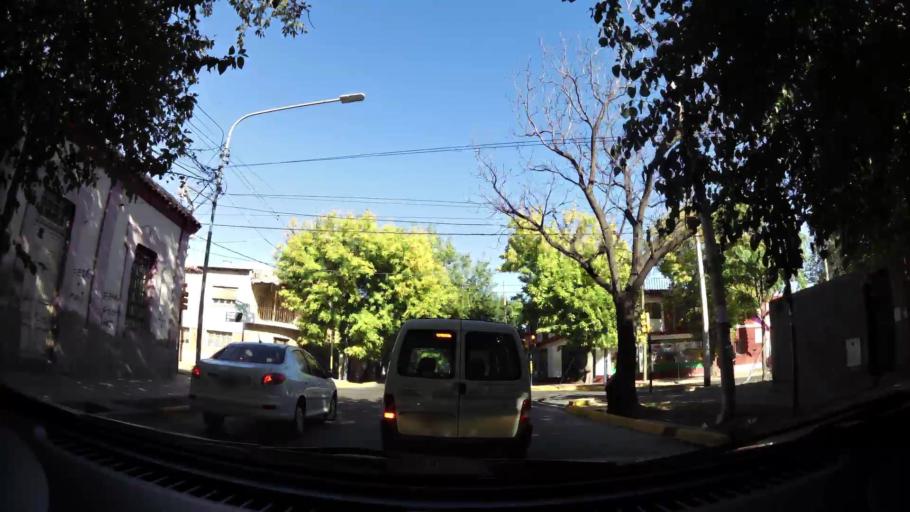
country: AR
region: Mendoza
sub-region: Departamento de Godoy Cruz
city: Godoy Cruz
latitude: -32.9238
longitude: -68.8540
